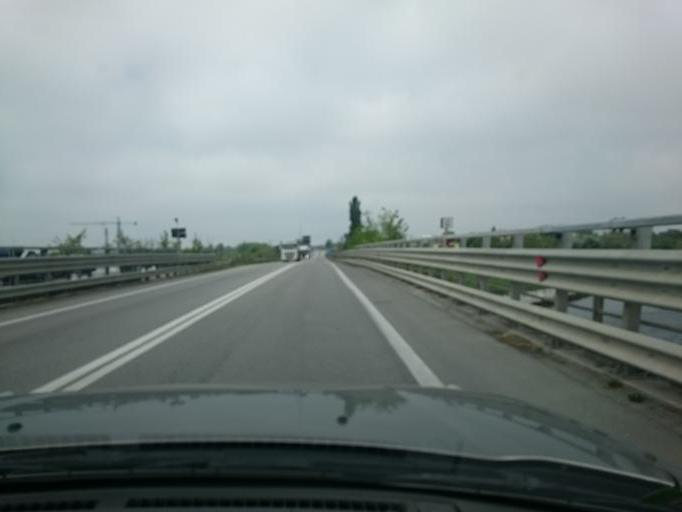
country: IT
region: Veneto
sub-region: Provincia di Venezia
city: Sant'Anna
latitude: 45.1907
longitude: 12.2761
